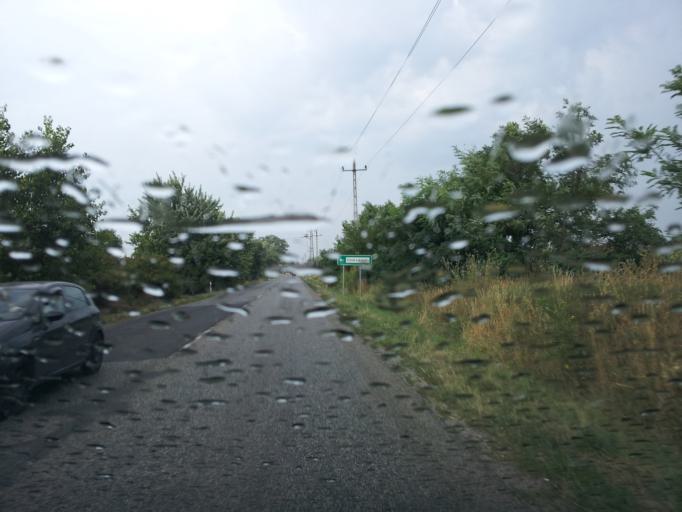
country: HU
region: Pest
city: Taksony
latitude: 47.3140
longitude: 19.0418
